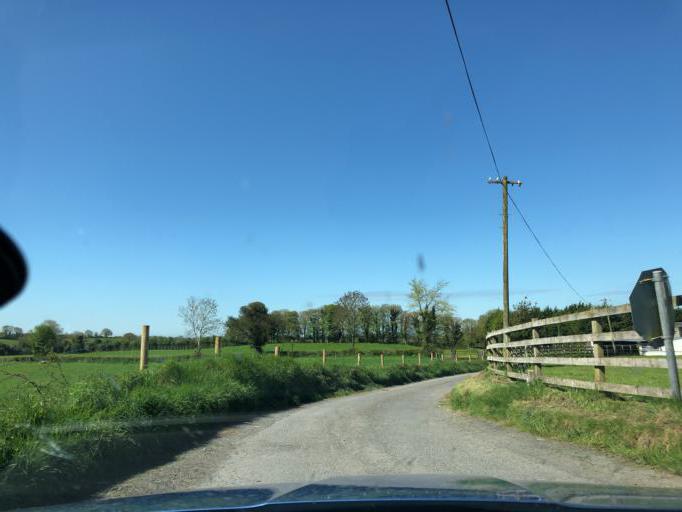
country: IE
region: Connaught
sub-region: County Galway
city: Portumna
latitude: 53.1502
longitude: -8.2925
